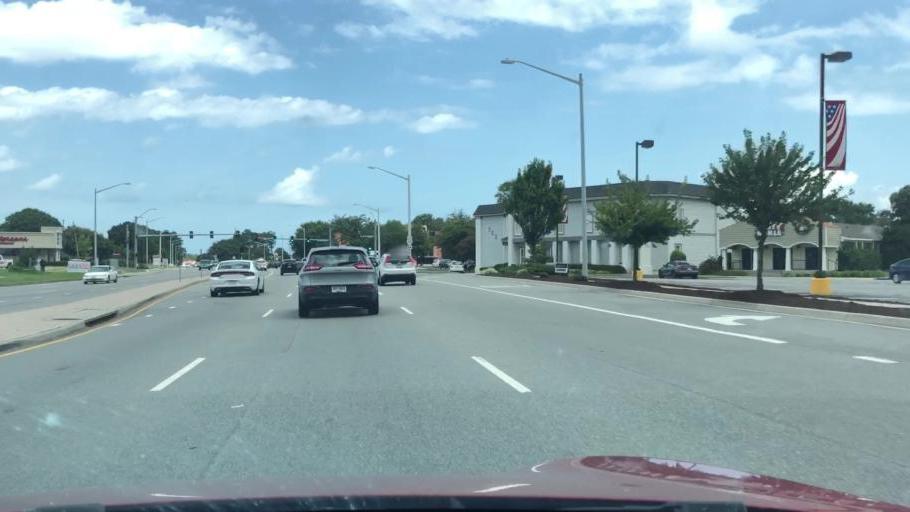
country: US
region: Virginia
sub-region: City of Chesapeake
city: Chesapeake
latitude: 36.8642
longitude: -76.1318
